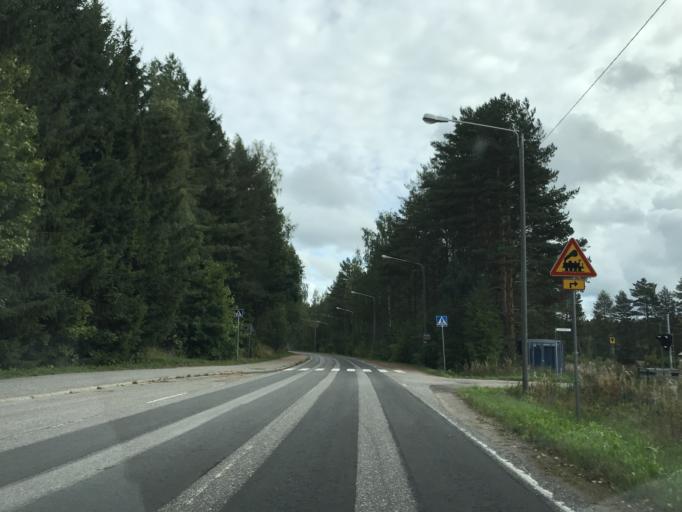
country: FI
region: Paijanne Tavastia
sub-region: Lahti
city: Nastola
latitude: 61.0114
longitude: 25.8058
